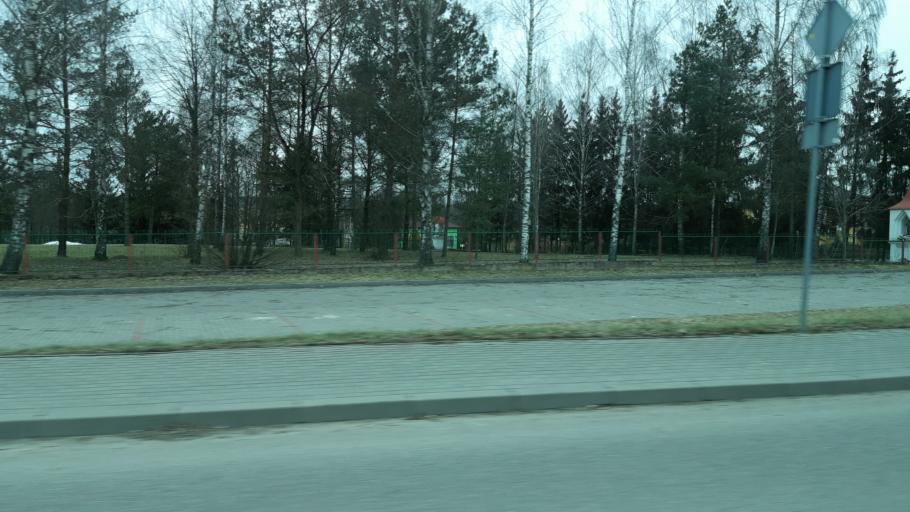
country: PL
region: Podlasie
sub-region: Suwalki
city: Suwalki
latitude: 54.3221
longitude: 22.9716
